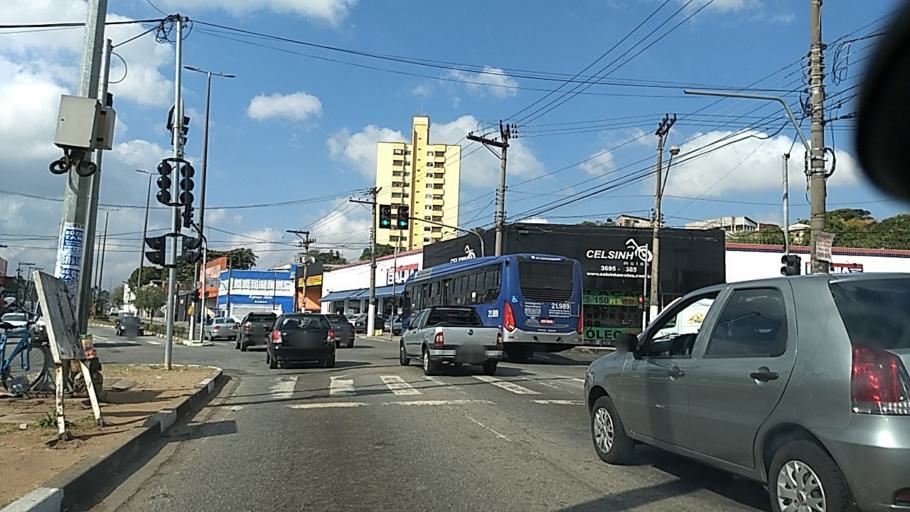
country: BR
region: Sao Paulo
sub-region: Osasco
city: Osasco
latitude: -23.5246
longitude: -46.8120
